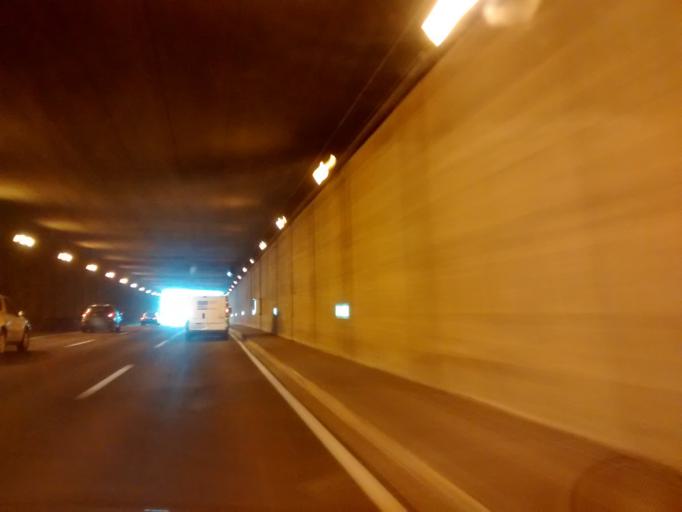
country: ES
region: Catalonia
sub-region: Provincia de Barcelona
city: Nou Barris
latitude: 41.4465
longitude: 2.1827
